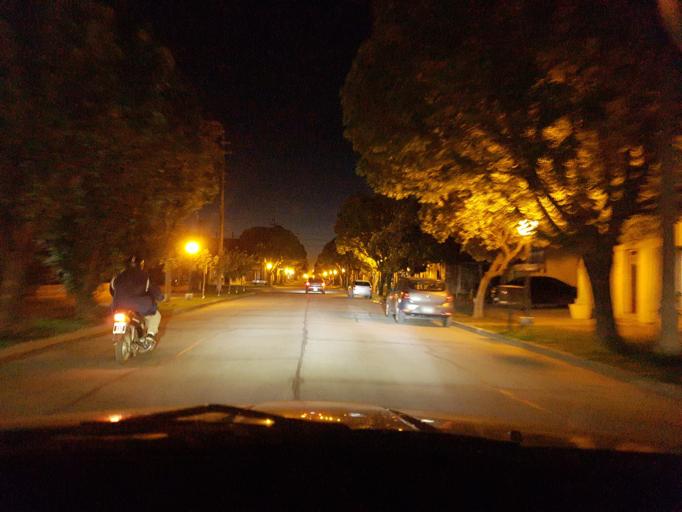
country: AR
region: Cordoba
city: General Cabrera
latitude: -32.7595
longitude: -63.7945
